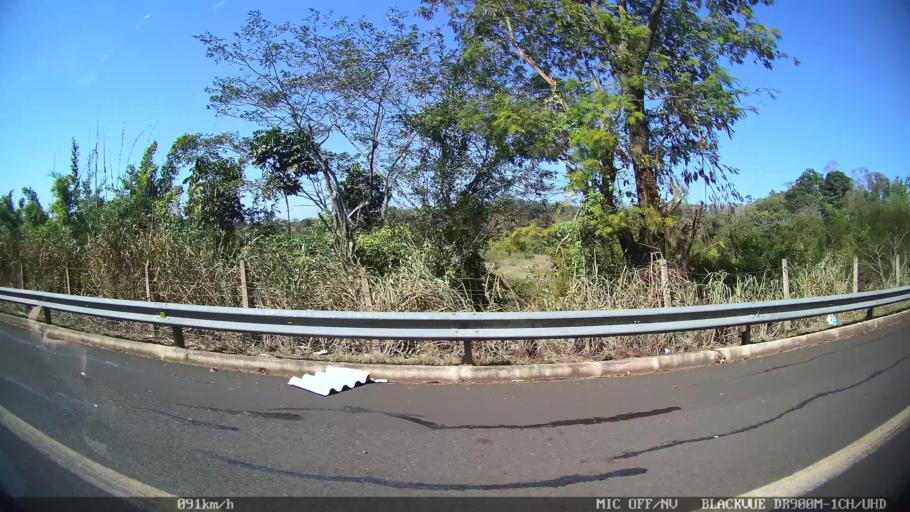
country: BR
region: Sao Paulo
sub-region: Batatais
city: Batatais
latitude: -20.7330
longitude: -47.5261
